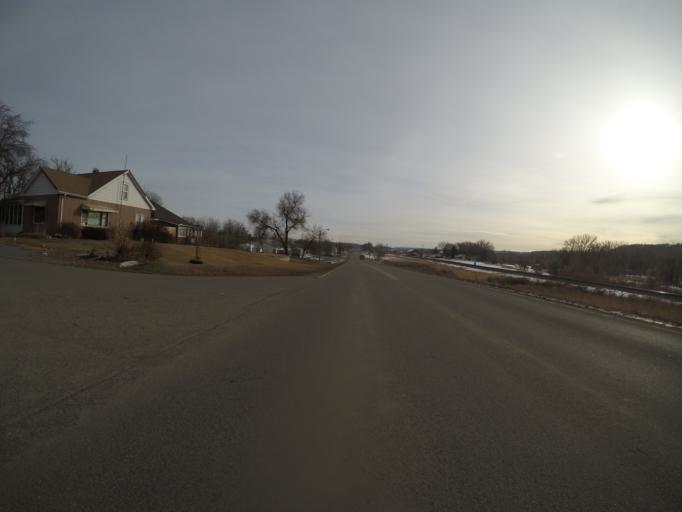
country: US
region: Montana
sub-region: Stillwater County
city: Columbus
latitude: 45.6386
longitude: -109.2601
